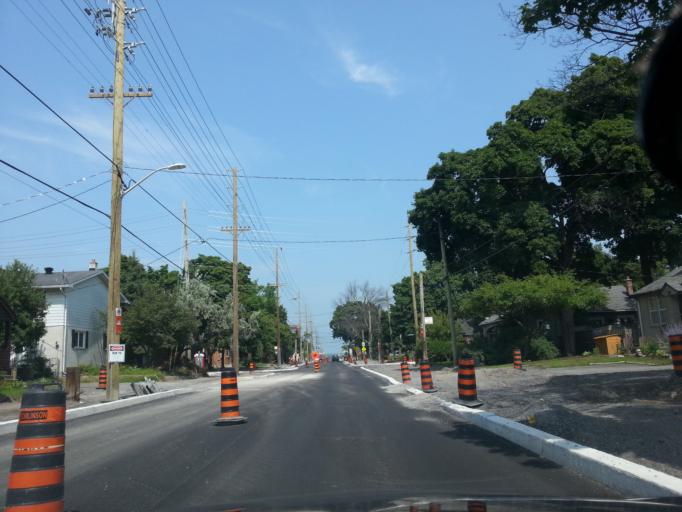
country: CA
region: Ontario
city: Ottawa
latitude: 45.3884
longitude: -75.7515
